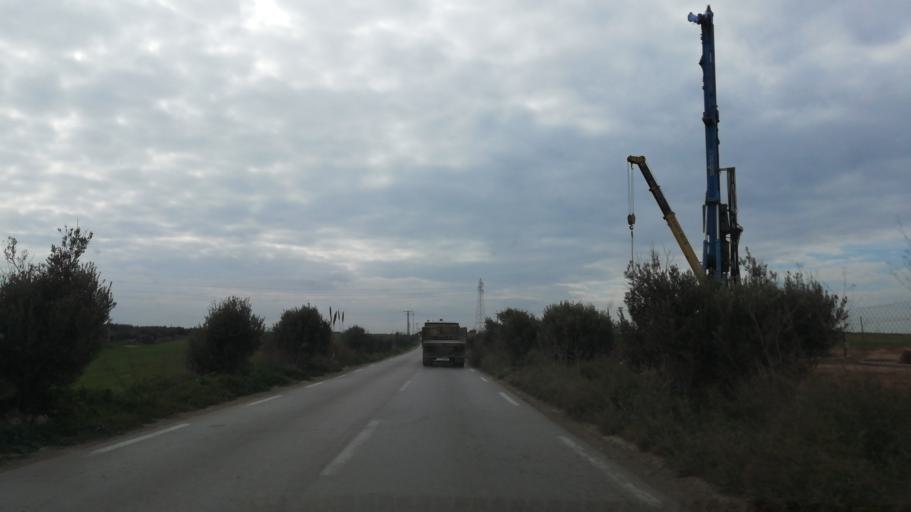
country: DZ
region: Oran
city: Ain el Bya
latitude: 35.7895
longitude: -0.3425
